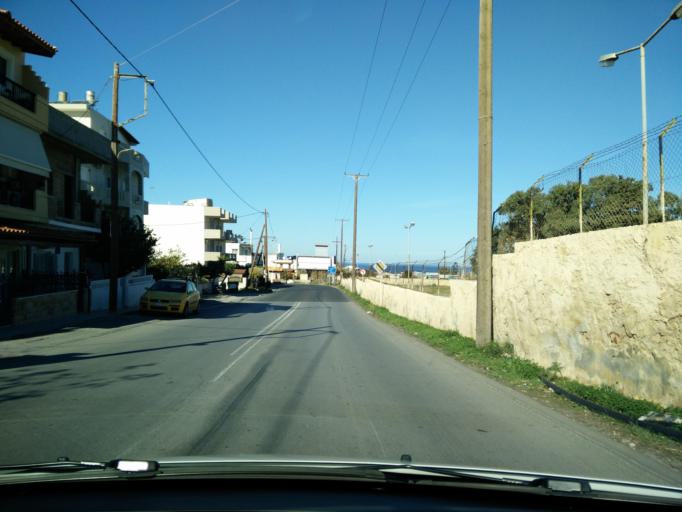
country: GR
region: Crete
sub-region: Nomos Irakleiou
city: Nea Alikarnassos
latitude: 35.3358
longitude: 25.1652
